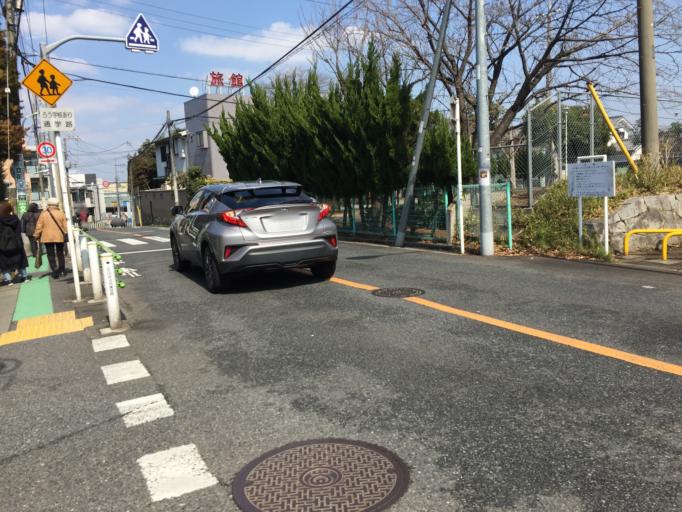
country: JP
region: Tokyo
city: Tokyo
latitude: 35.6679
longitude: 139.6415
